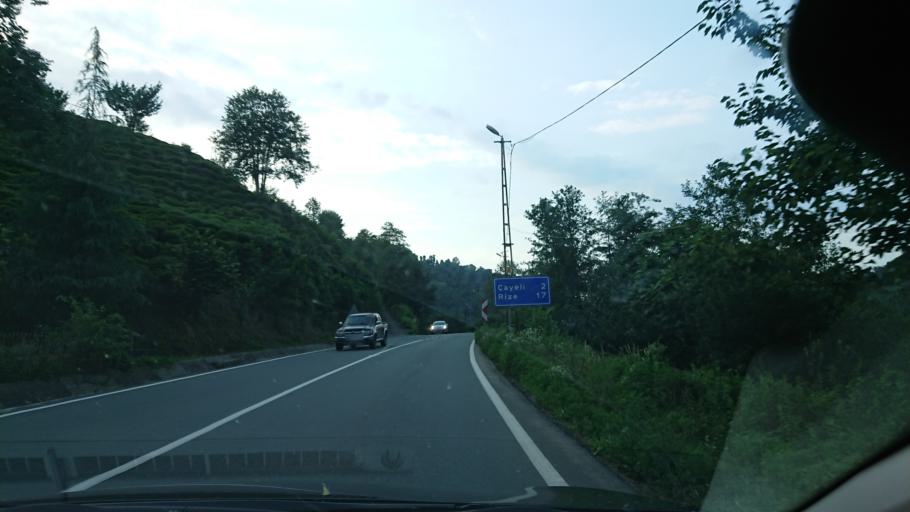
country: TR
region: Rize
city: Cayeli
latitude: 41.0673
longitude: 40.7138
